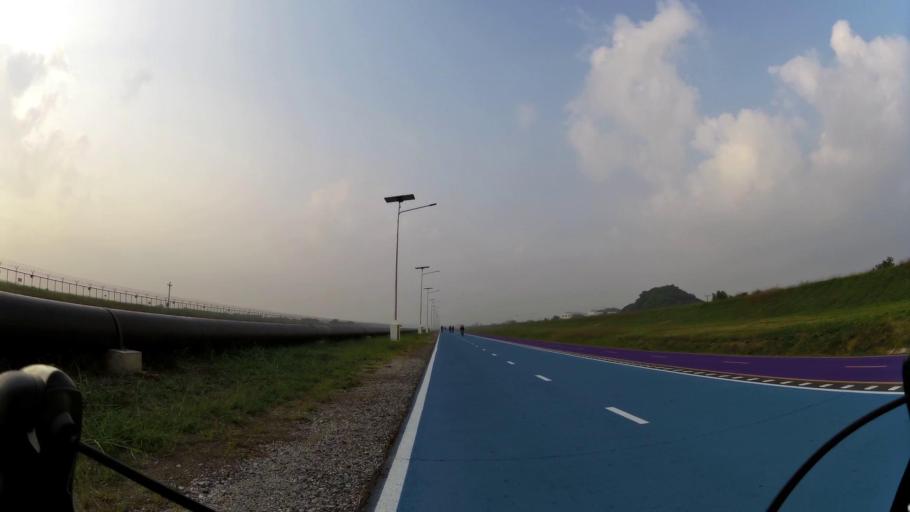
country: TH
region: Bangkok
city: Lat Krabang
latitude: 13.6881
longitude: 100.7689
